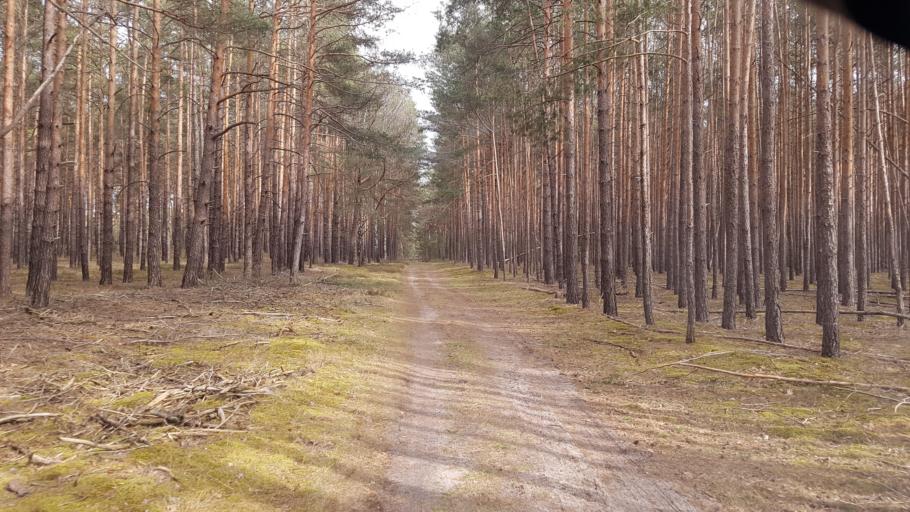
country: DE
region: Brandenburg
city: Finsterwalde
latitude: 51.5673
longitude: 13.6840
